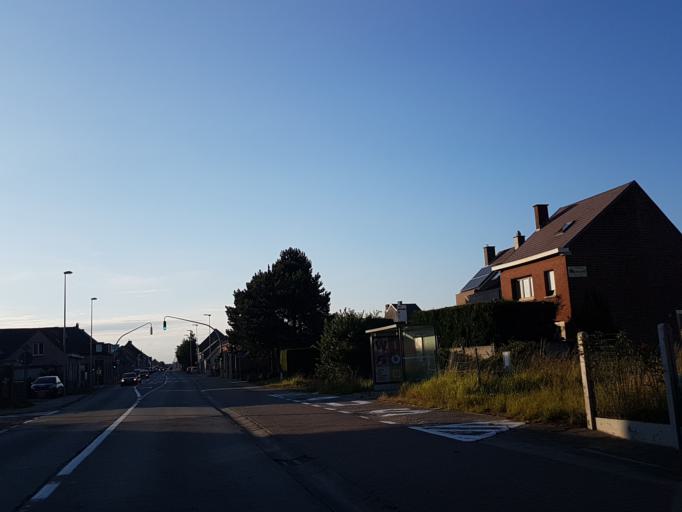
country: BE
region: Flanders
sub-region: Provincie Oost-Vlaanderen
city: Lebbeke
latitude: 50.9815
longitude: 4.1414
